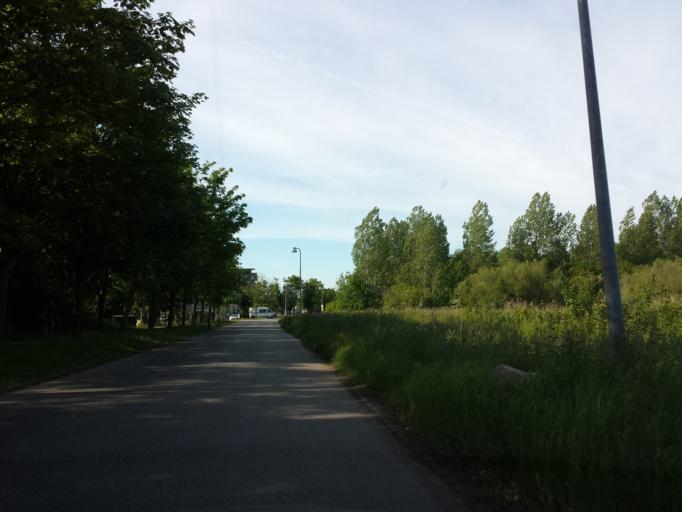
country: DK
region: Capital Region
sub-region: Ballerup Kommune
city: Ballerup
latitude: 55.7177
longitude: 12.3752
